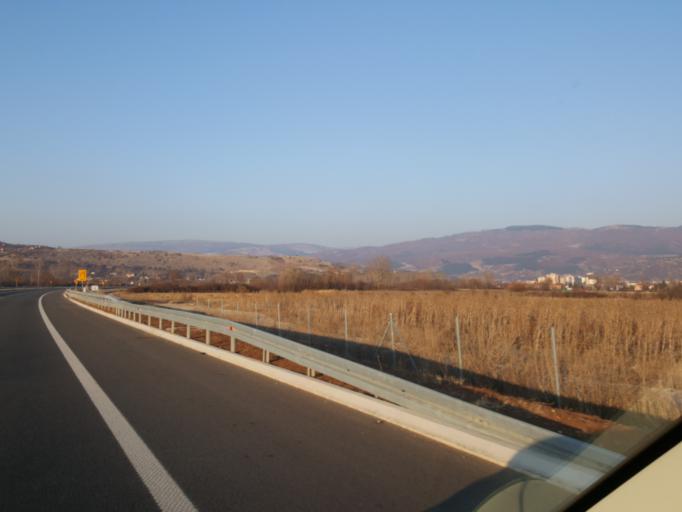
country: RS
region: Central Serbia
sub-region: Pirotski Okrug
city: Pirot
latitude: 43.1446
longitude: 22.5676
